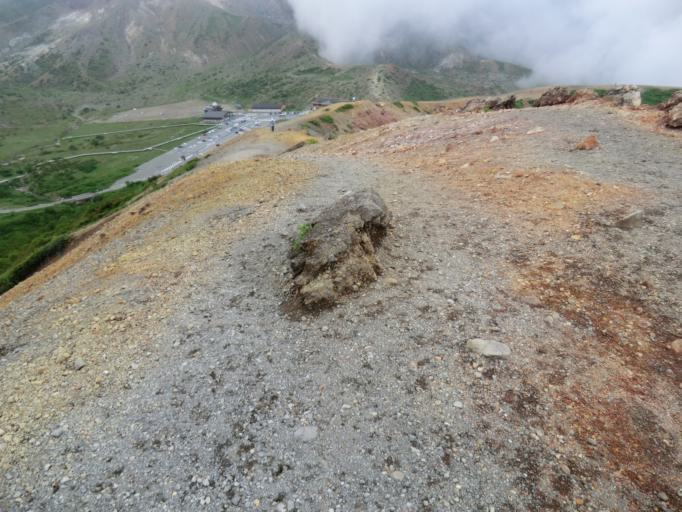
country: JP
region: Fukushima
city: Fukushima-shi
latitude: 37.7204
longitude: 140.2600
